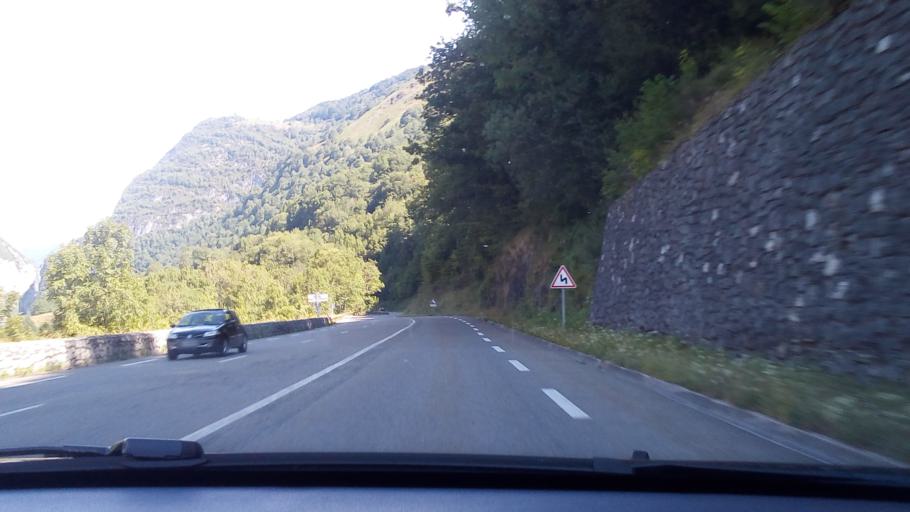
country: ES
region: Aragon
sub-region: Provincia de Huesca
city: Canfranc
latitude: 42.8650
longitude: -0.5498
